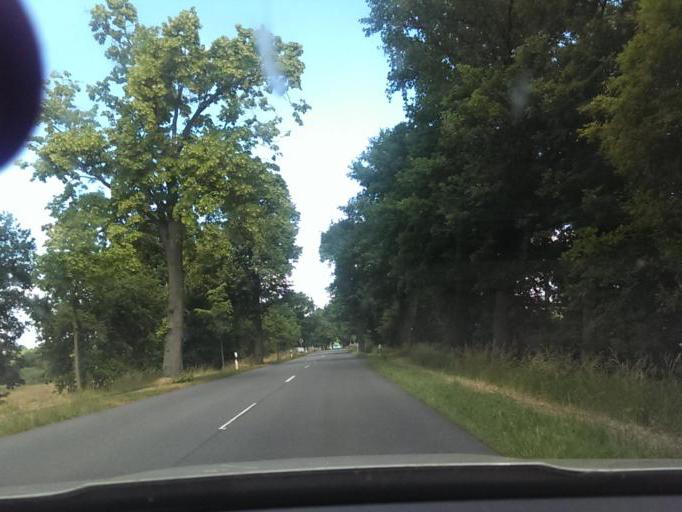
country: DE
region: Lower Saxony
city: Hellwege
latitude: 53.0764
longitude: 9.2311
